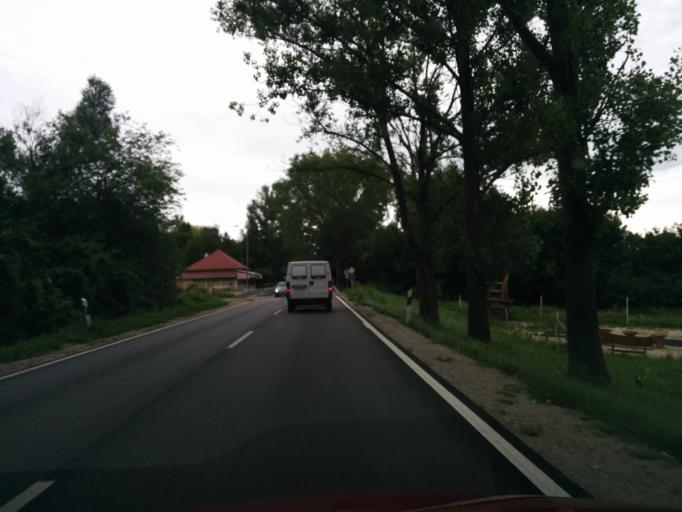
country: HU
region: Gyor-Moson-Sopron
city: Sopron
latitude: 47.7180
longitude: 16.5685
